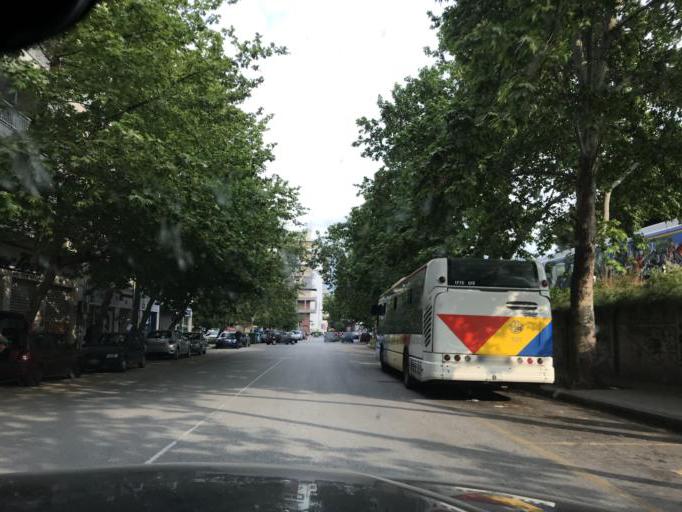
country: GR
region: Central Macedonia
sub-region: Nomos Thessalonikis
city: Thessaloniki
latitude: 40.6450
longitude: 22.9307
